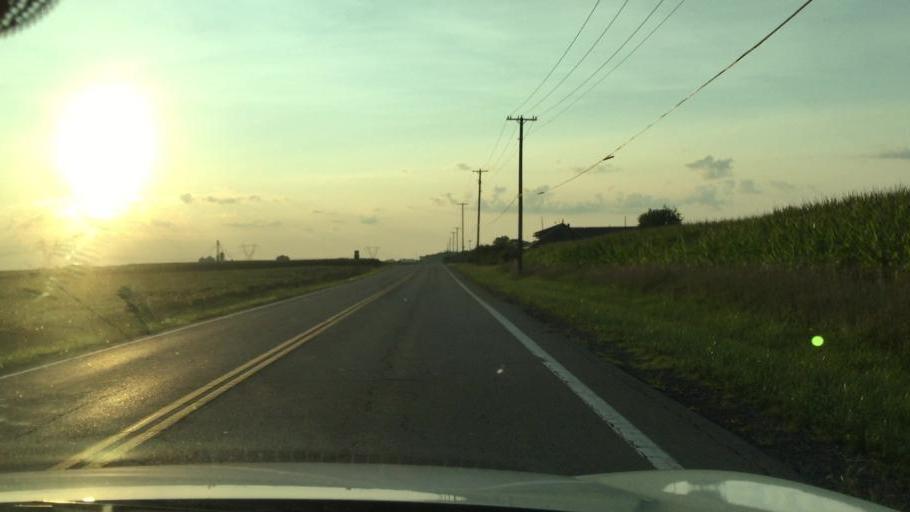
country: US
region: Ohio
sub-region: Madison County
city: West Jefferson
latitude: 39.9673
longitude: -83.3641
